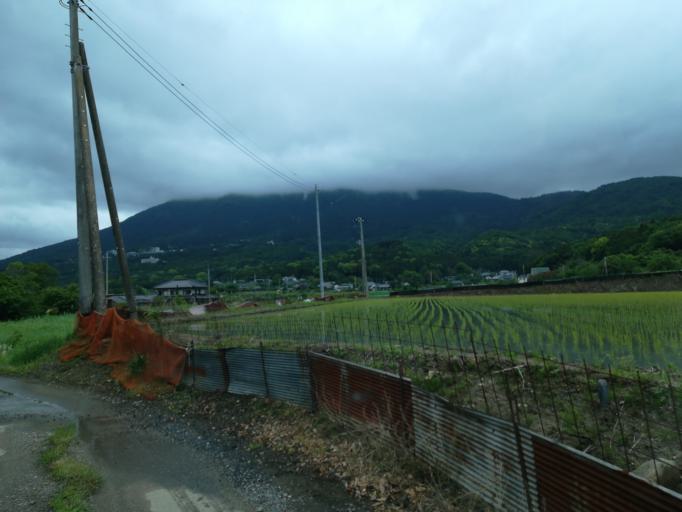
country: JP
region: Ibaraki
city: Tsukuba
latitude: 36.1933
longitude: 140.1109
